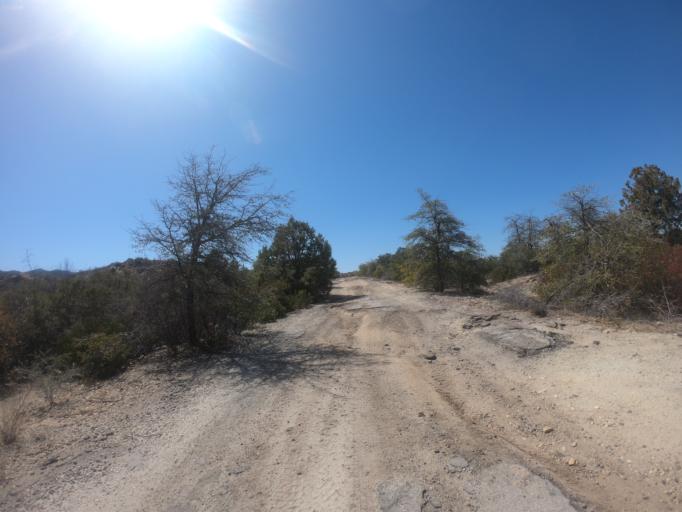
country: US
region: Arizona
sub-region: Gila County
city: Miami
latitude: 33.3553
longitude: -110.9637
